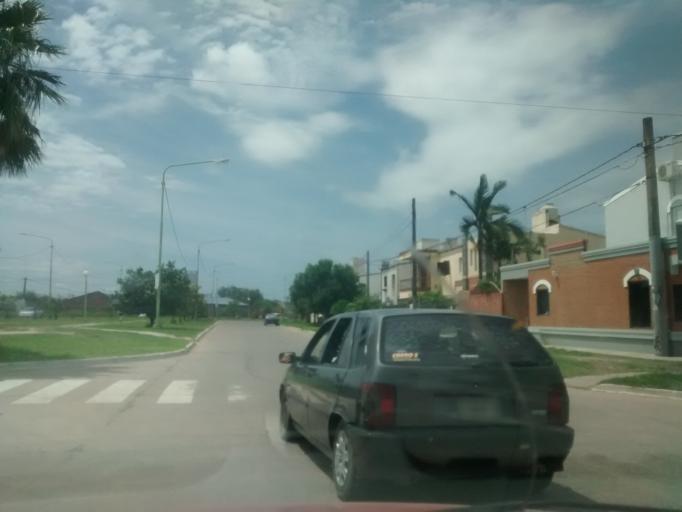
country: AR
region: Chaco
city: Resistencia
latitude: -27.4655
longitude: -58.9883
